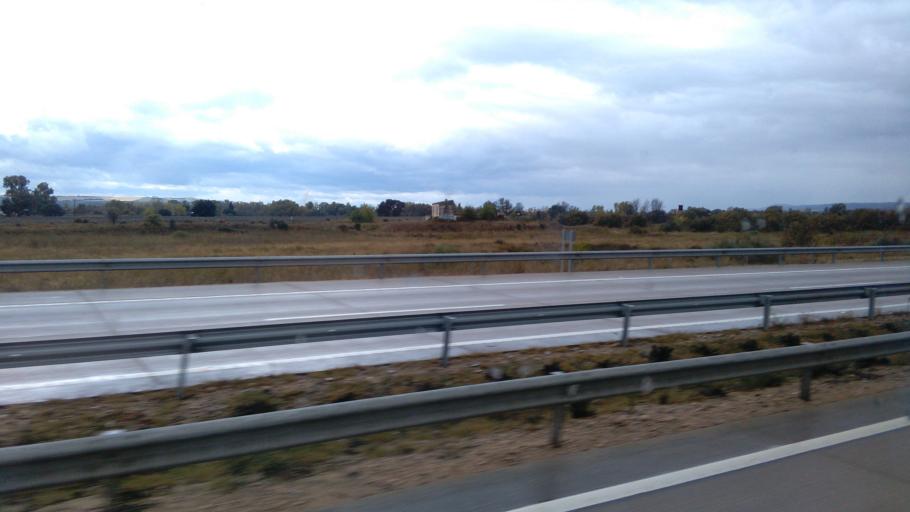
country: ES
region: Castille-La Mancha
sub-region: Province of Toledo
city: Cazalegas
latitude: 39.9826
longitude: -4.7517
